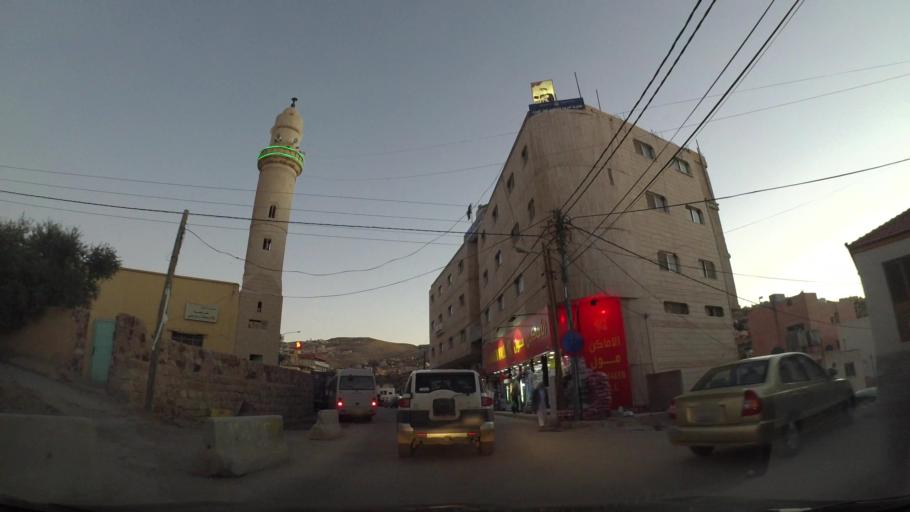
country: JO
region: Ma'an
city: Petra
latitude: 30.3202
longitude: 35.4795
